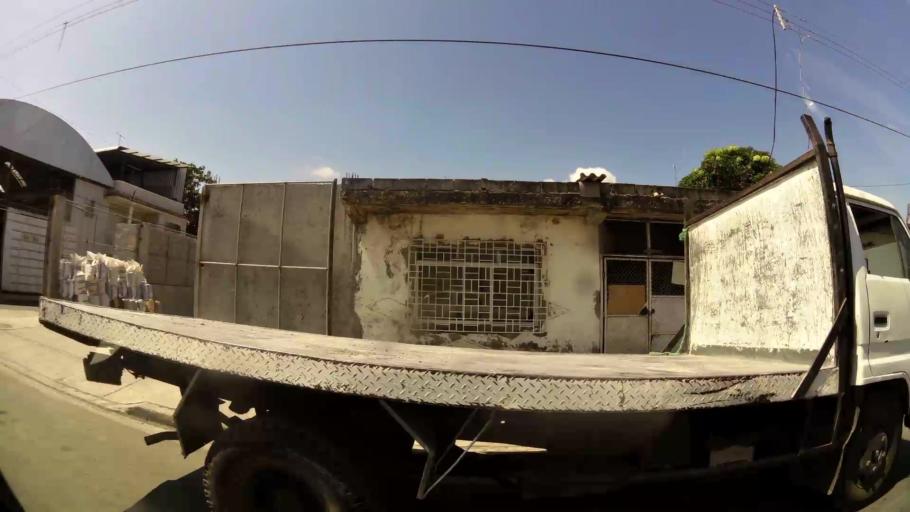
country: EC
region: Guayas
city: Guayaquil
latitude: -2.2315
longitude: -79.9199
